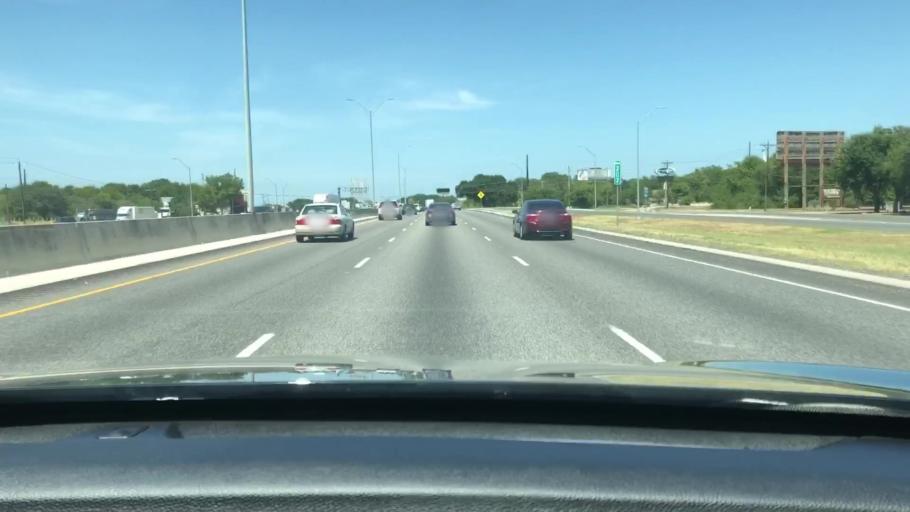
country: US
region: Texas
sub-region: Hays County
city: San Marcos
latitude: 29.8988
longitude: -97.9076
